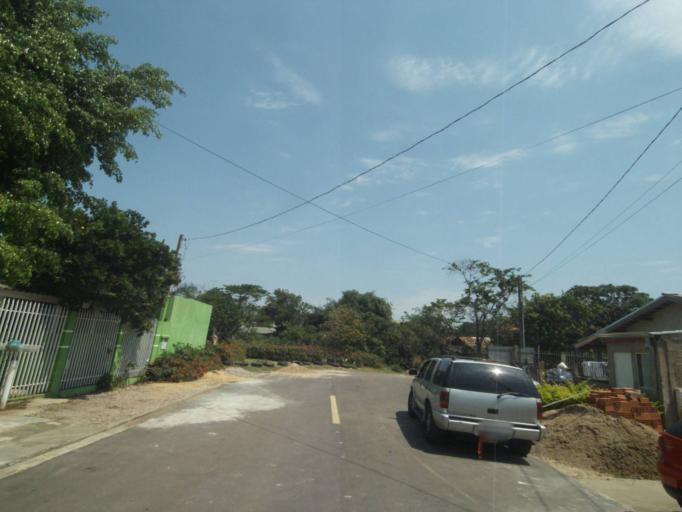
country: BR
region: Parana
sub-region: Sao Jose Dos Pinhais
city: Sao Jose dos Pinhais
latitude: -25.5191
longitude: -49.2695
